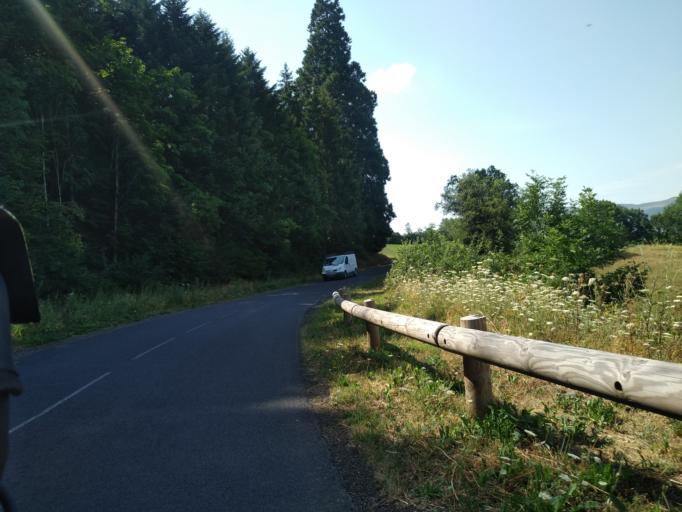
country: FR
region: Auvergne
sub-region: Departement du Cantal
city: Riom-es-Montagnes
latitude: 45.1978
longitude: 2.7174
